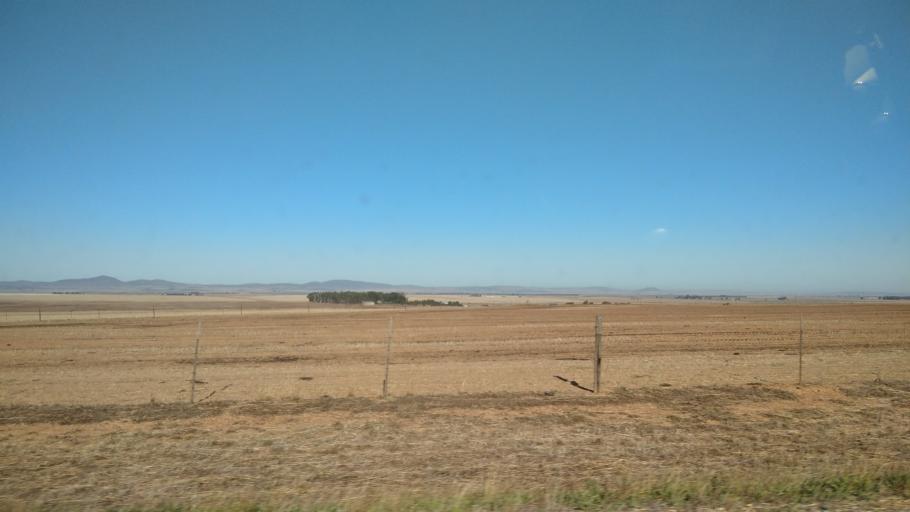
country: ZA
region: Western Cape
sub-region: West Coast District Municipality
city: Malmesbury
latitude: -33.3271
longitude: 18.6293
